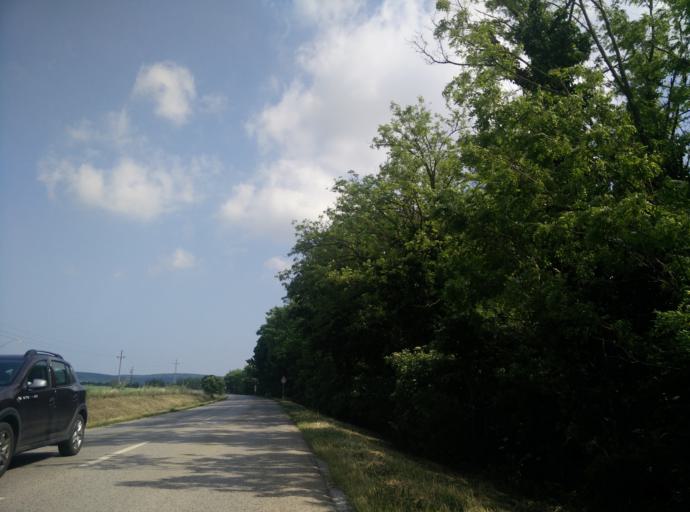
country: HU
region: Pest
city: Biatorbagy
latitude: 47.4762
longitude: 18.7929
